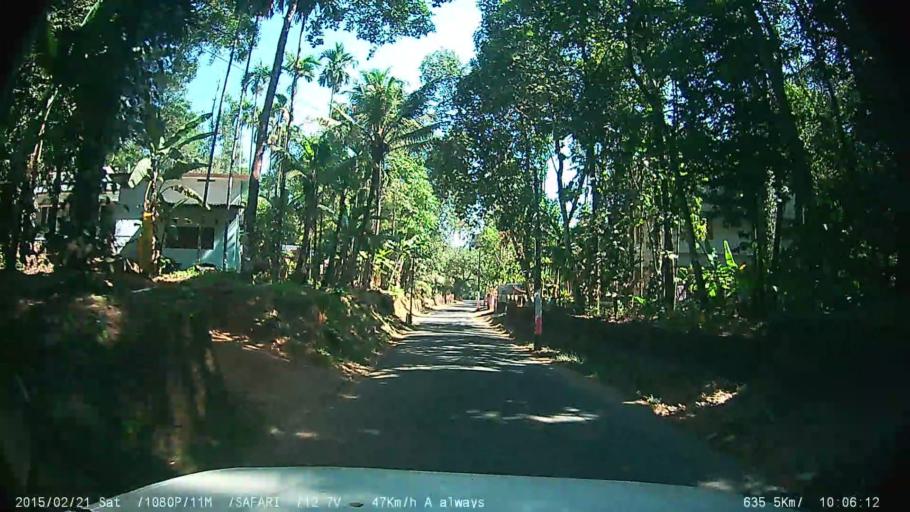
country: IN
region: Kerala
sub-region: Ernakulam
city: Piravam
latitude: 9.8656
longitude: 76.6078
